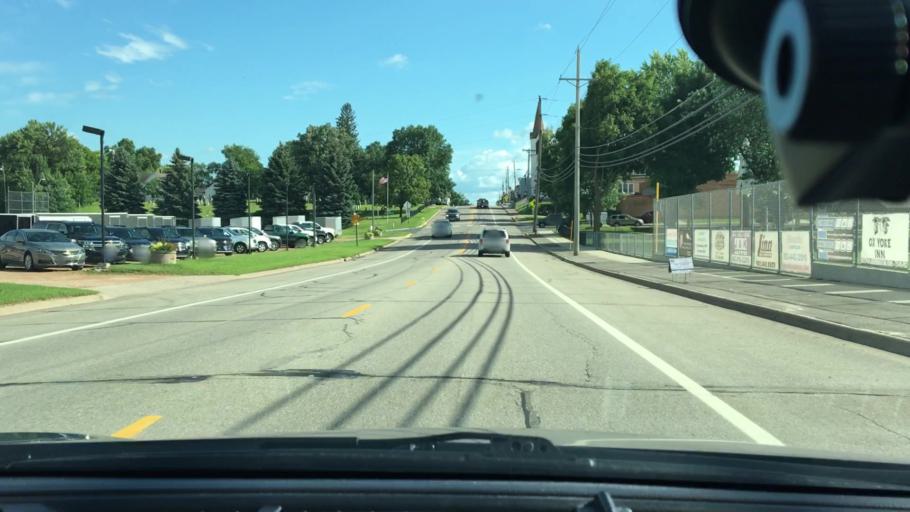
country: US
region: Minnesota
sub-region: Hennepin County
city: Saint Bonifacius
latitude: 44.9066
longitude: -93.7473
